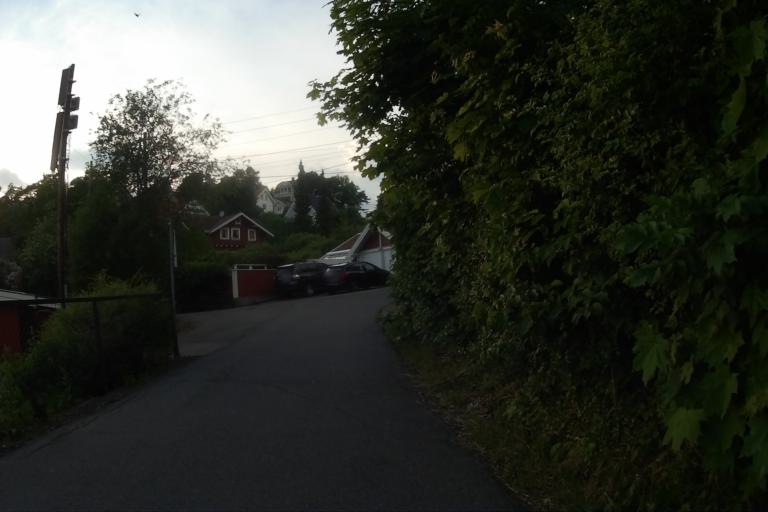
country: NO
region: Oslo
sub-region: Oslo
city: Oslo
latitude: 59.8775
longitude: 10.7753
